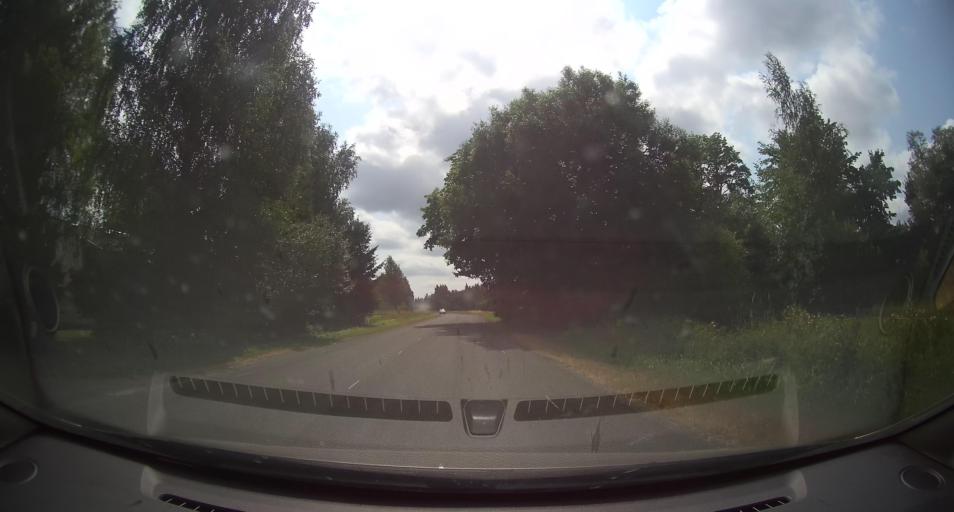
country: EE
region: Paernumaa
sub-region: Audru vald
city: Audru
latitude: 58.4431
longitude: 24.3066
